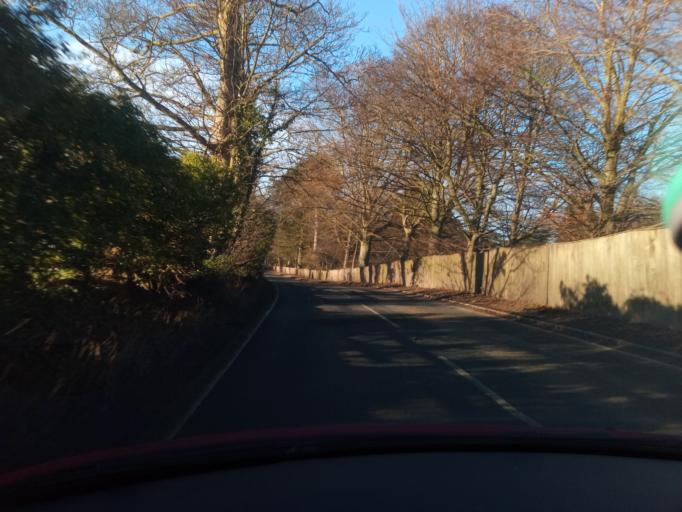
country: GB
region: England
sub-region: North Yorkshire
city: Ripon
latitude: 54.2152
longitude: -1.4510
